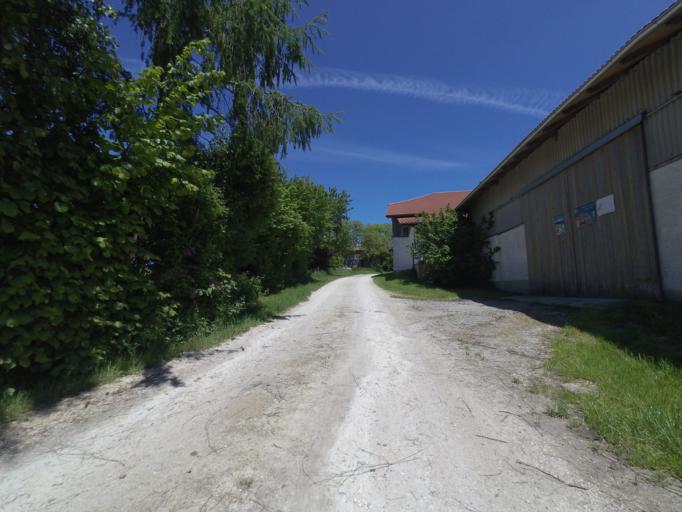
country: DE
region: Bavaria
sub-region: Upper Bavaria
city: Waging am See
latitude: 47.9516
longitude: 12.7768
